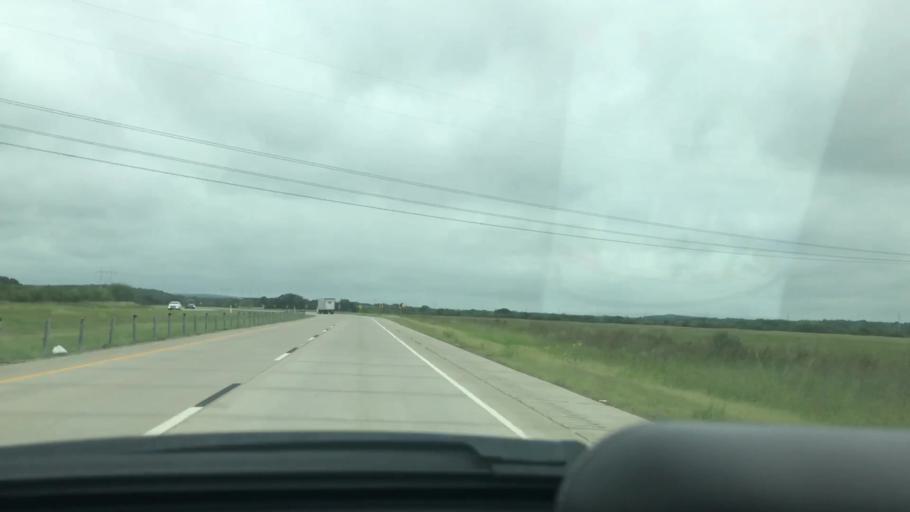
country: US
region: Oklahoma
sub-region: Pittsburg County
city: McAlester
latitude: 34.6889
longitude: -95.9155
